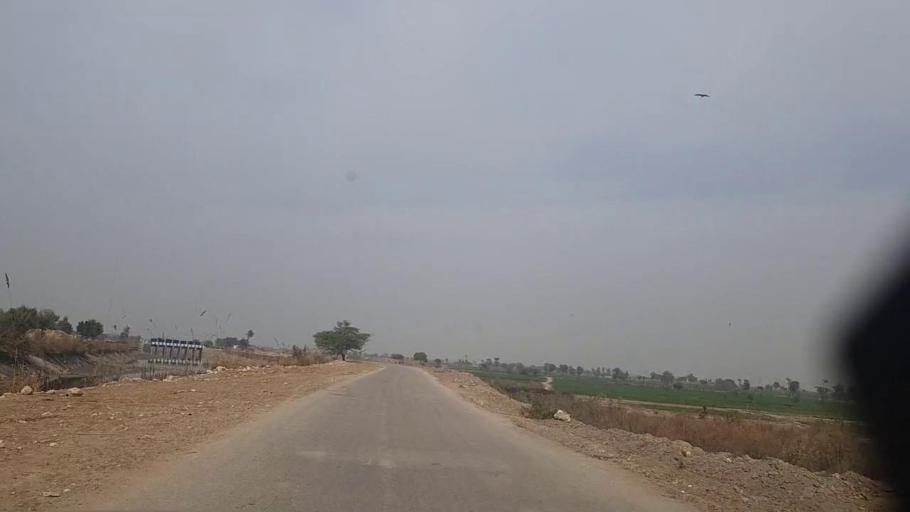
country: PK
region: Sindh
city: Sakrand
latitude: 26.2809
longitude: 68.2276
